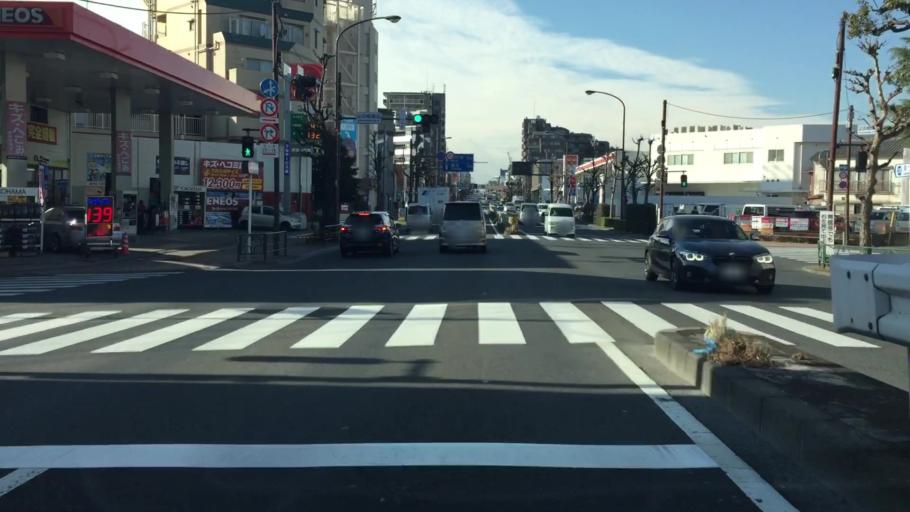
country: JP
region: Saitama
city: Kawaguchi
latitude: 35.7530
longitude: 139.6852
